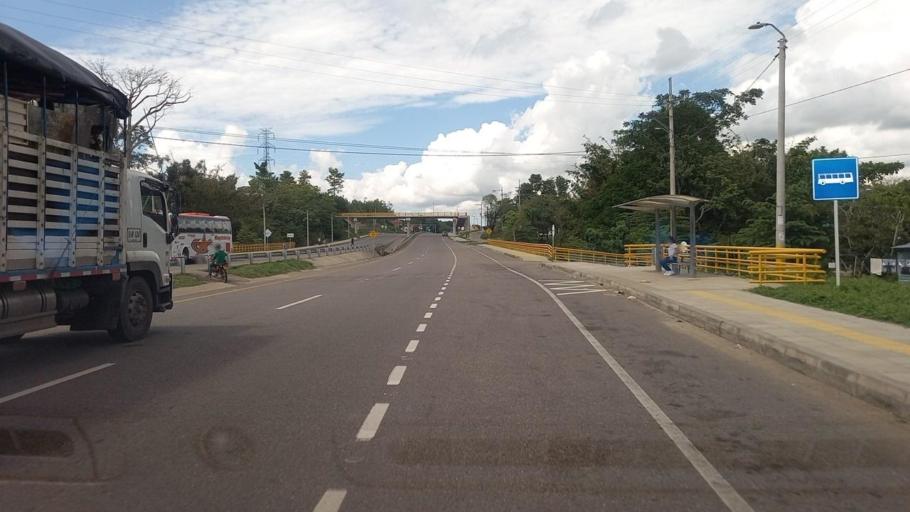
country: CO
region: Santander
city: Sabana de Torres
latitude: 7.1334
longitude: -73.5538
